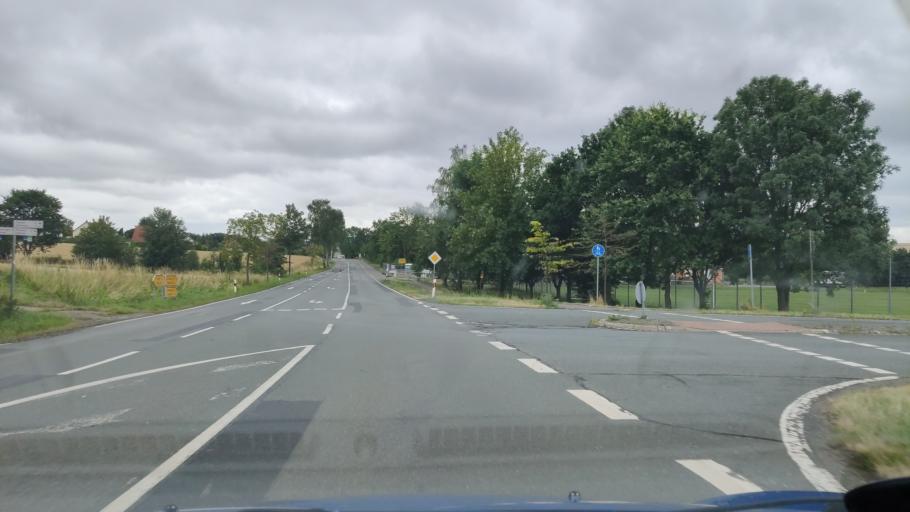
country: DE
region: Lower Saxony
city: Coppenbrugge
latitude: 52.0949
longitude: 9.4940
